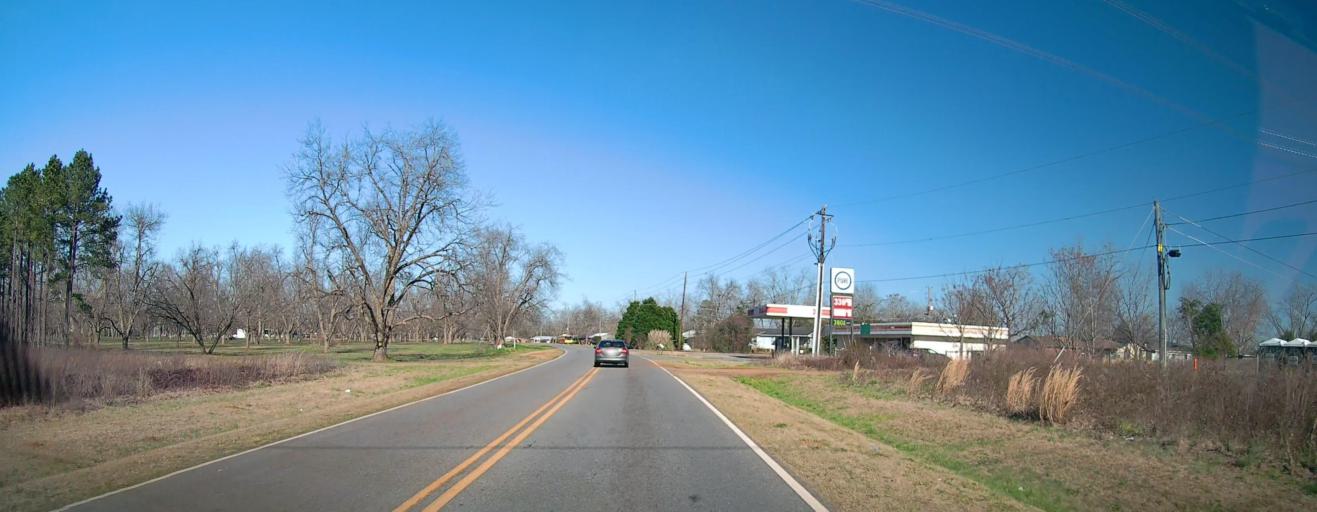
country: US
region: Georgia
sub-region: Sumter County
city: Americus
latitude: 32.0987
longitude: -84.2120
